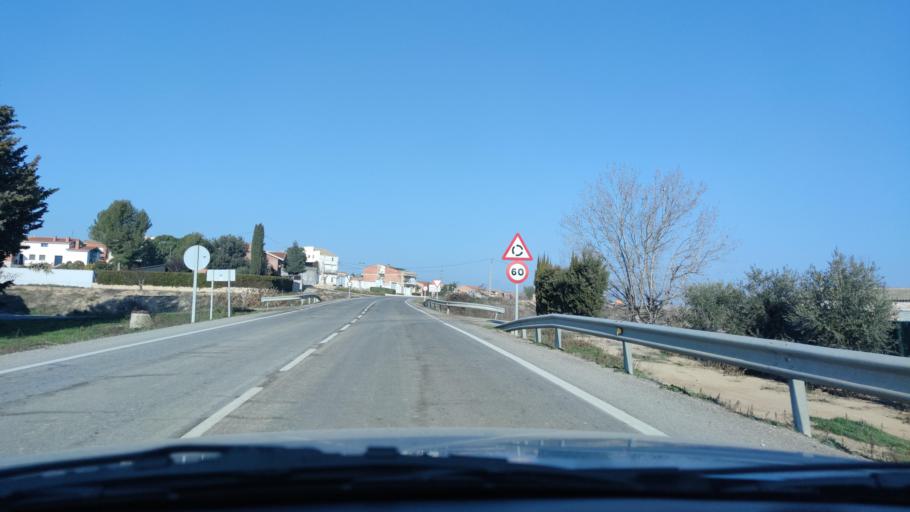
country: ES
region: Catalonia
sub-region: Provincia de Lleida
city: Torrefarrera
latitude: 41.6972
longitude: 0.6352
